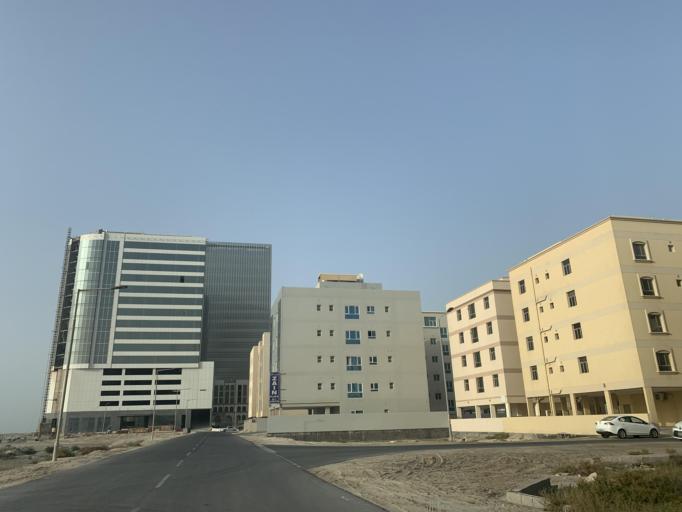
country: BH
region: Manama
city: Jidd Hafs
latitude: 26.2413
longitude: 50.5301
